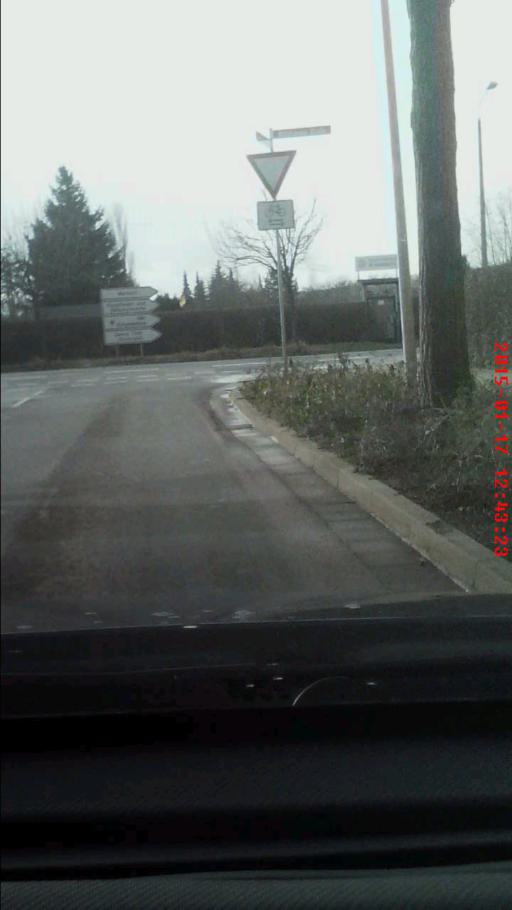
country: DE
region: Thuringia
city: Erfurt
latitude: 50.9875
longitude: 11.0123
